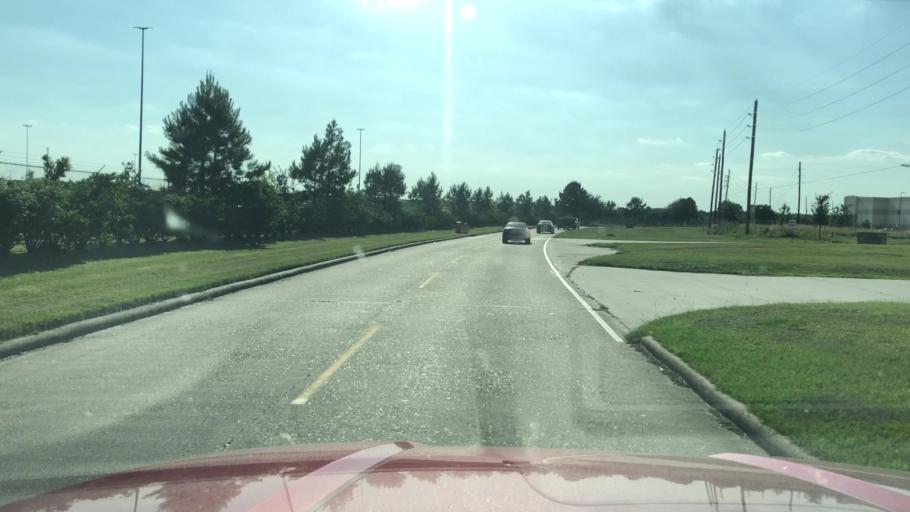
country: US
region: Texas
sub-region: Harris County
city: Hudson
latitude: 29.9423
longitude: -95.4885
